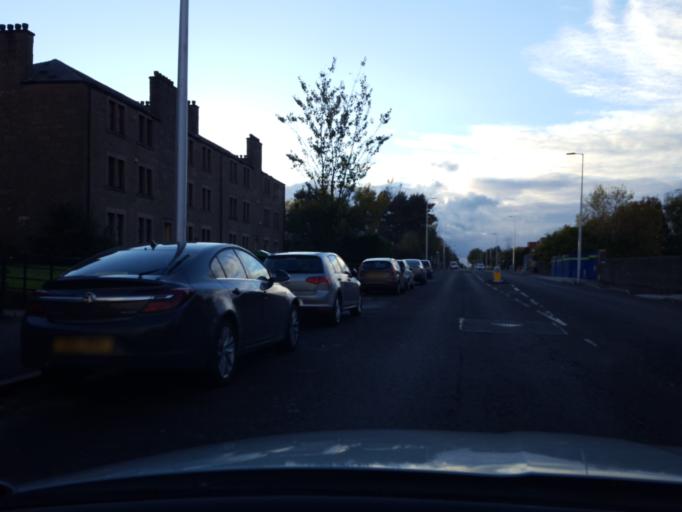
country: GB
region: Scotland
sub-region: Dundee City
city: Dundee
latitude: 56.4750
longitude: -2.9873
